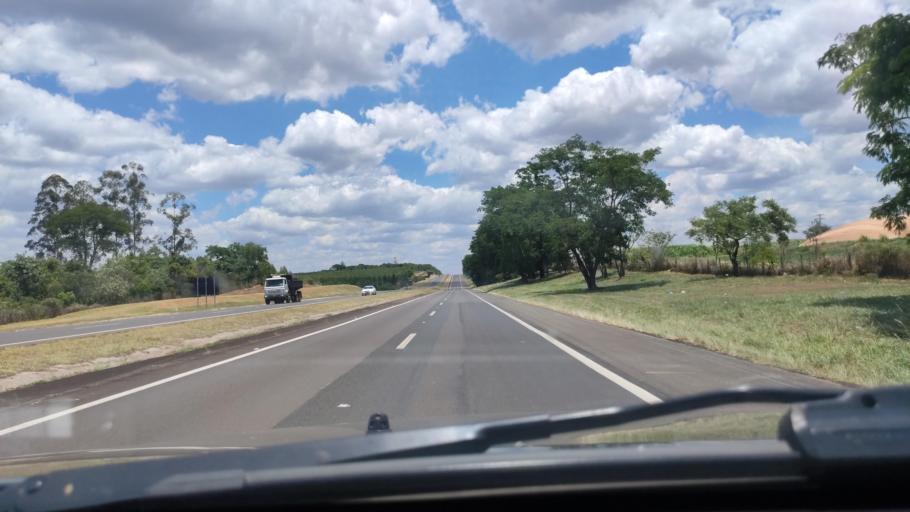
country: BR
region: Sao Paulo
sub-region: Duartina
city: Duartina
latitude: -22.5051
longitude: -49.2866
